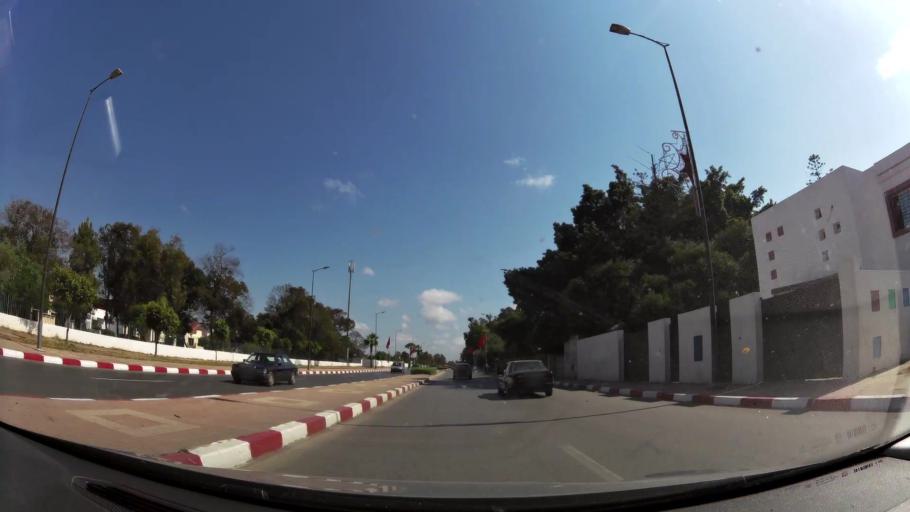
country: MA
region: Rabat-Sale-Zemmour-Zaer
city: Sale
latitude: 34.0408
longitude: -6.7750
